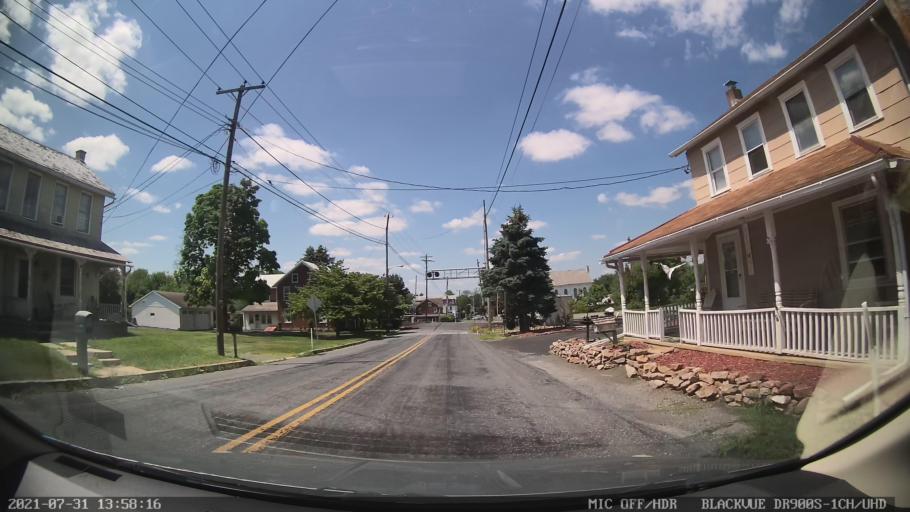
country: US
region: Pennsylvania
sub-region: Berks County
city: Topton
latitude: 40.5063
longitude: -75.6662
